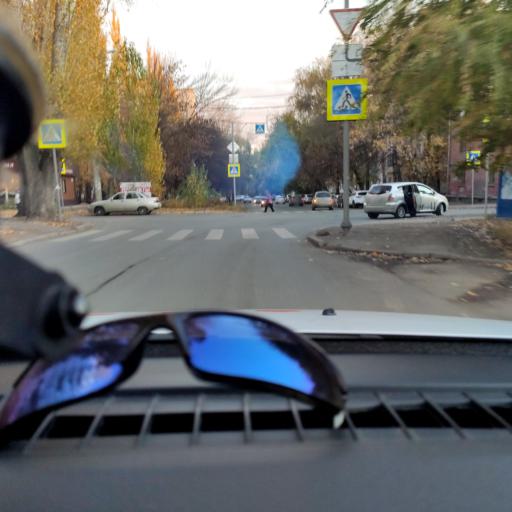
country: RU
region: Samara
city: Samara
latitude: 53.2352
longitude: 50.2463
